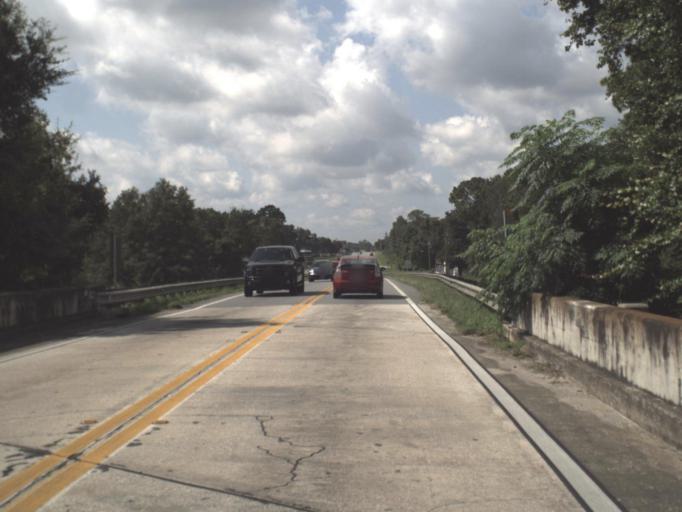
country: US
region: Florida
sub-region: Citrus County
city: Inverness
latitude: 28.8506
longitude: -82.3446
